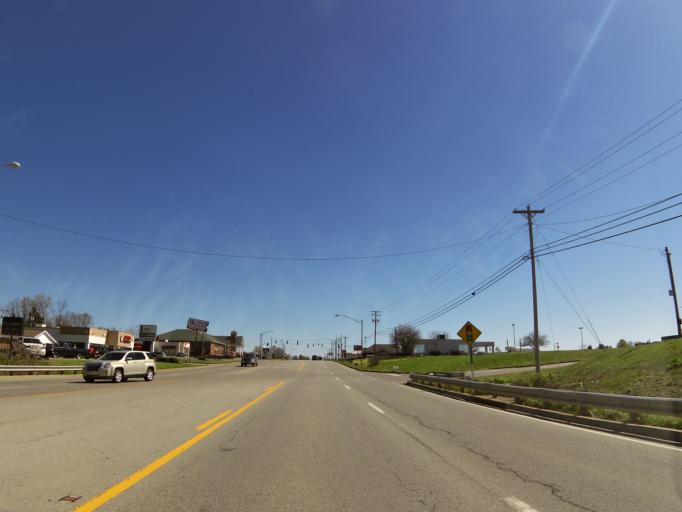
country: US
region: Kentucky
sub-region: Pulaski County
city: Somerset
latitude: 37.0990
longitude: -84.6222
